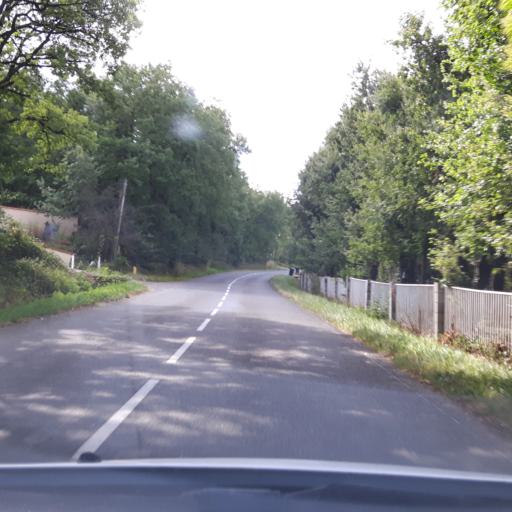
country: FR
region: Midi-Pyrenees
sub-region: Departement de la Haute-Garonne
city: Bouloc
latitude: 43.7956
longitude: 1.4132
